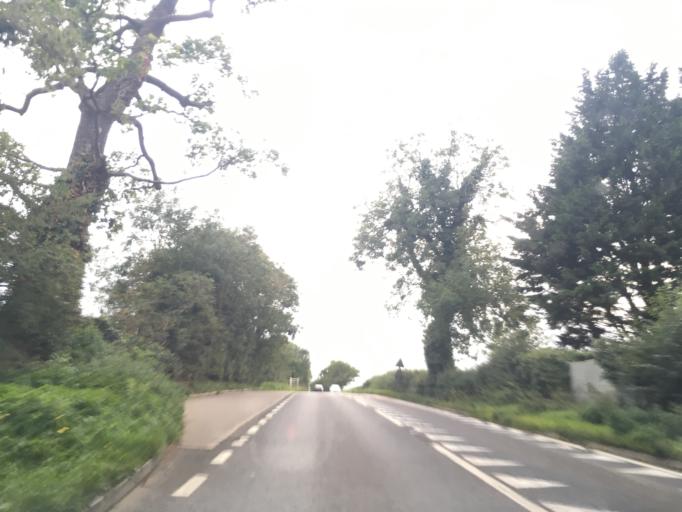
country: GB
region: England
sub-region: Oxfordshire
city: Claydon
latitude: 52.1135
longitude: -1.2858
